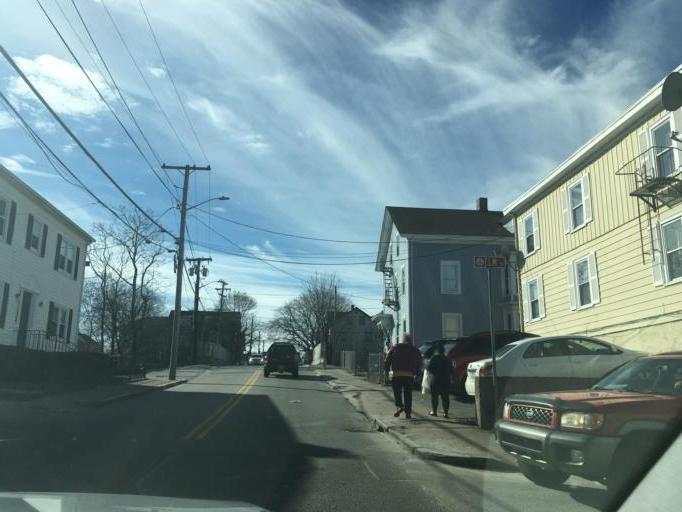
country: US
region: Rhode Island
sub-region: Providence County
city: Pawtucket
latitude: 41.8856
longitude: -71.3845
